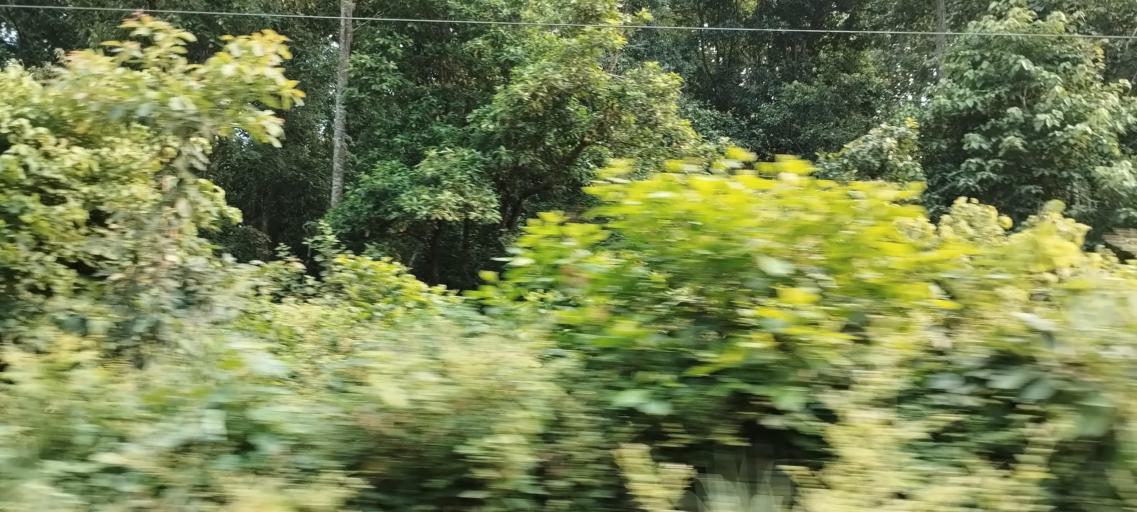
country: NP
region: Mid Western
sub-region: Bheri Zone
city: Bardiya
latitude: 28.4306
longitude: 81.3569
